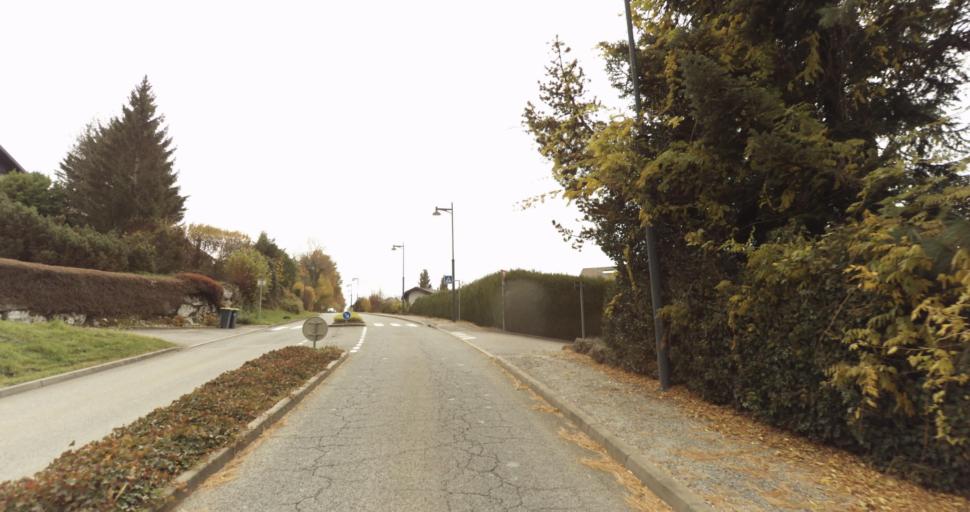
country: FR
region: Rhone-Alpes
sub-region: Departement de la Haute-Savoie
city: Annecy-le-Vieux
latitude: 45.9334
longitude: 6.1444
